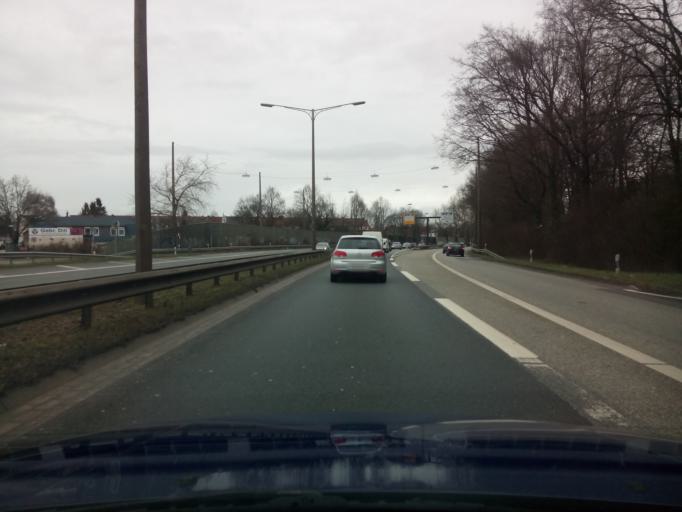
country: DE
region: Bremen
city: Bremen
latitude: 53.0978
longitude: 8.7955
